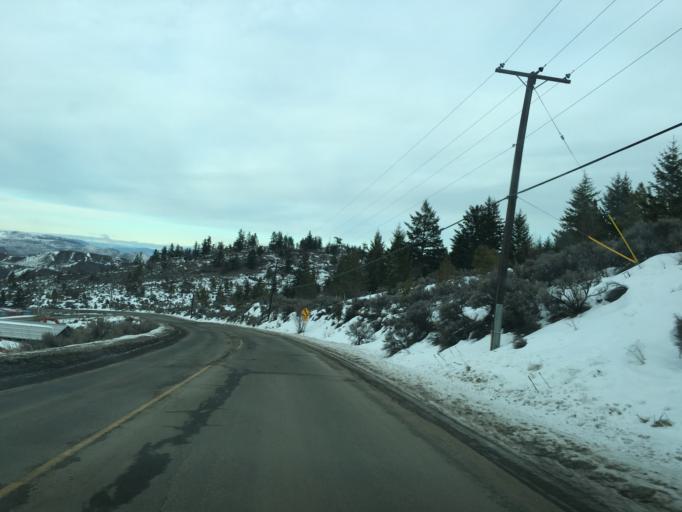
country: CA
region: British Columbia
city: Kamloops
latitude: 50.6576
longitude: -120.4363
